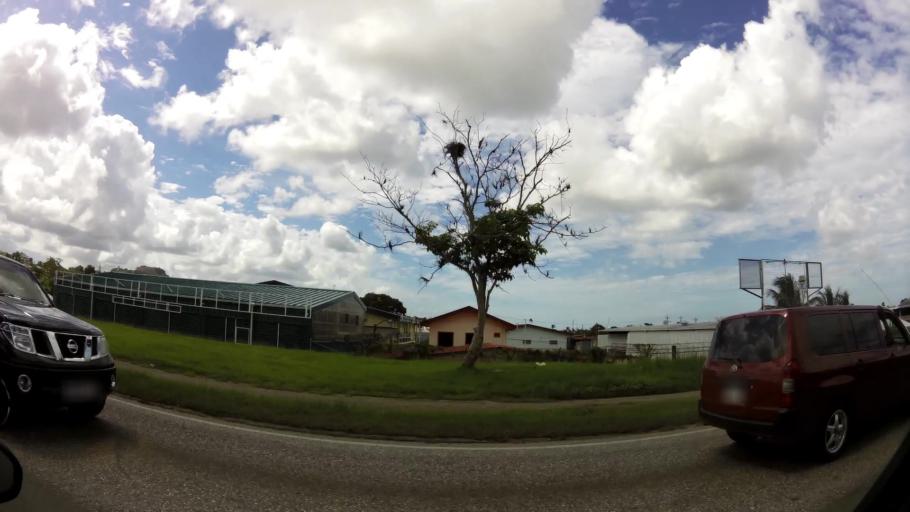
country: TT
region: City of San Fernando
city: Marabella
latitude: 10.2954
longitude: -61.4471
